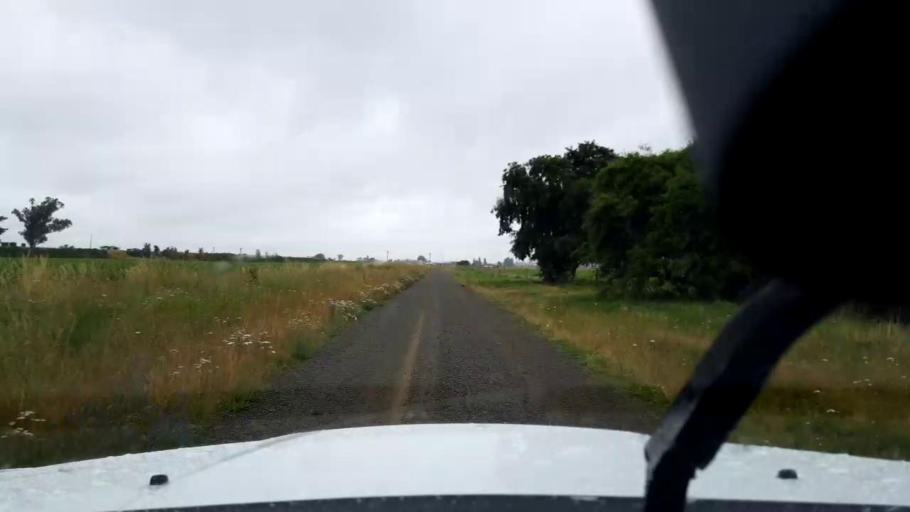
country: NZ
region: Canterbury
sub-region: Timaru District
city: Pleasant Point
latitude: -44.2537
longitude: 171.1956
